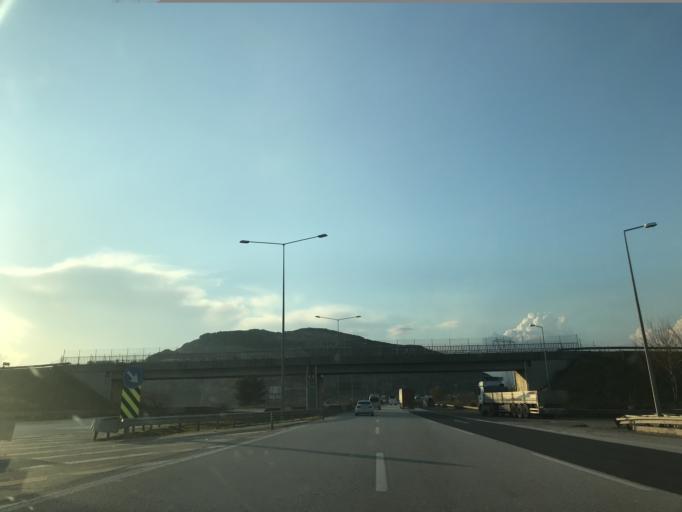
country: TR
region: Adana
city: Ceyhan
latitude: 36.9893
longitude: 35.7485
